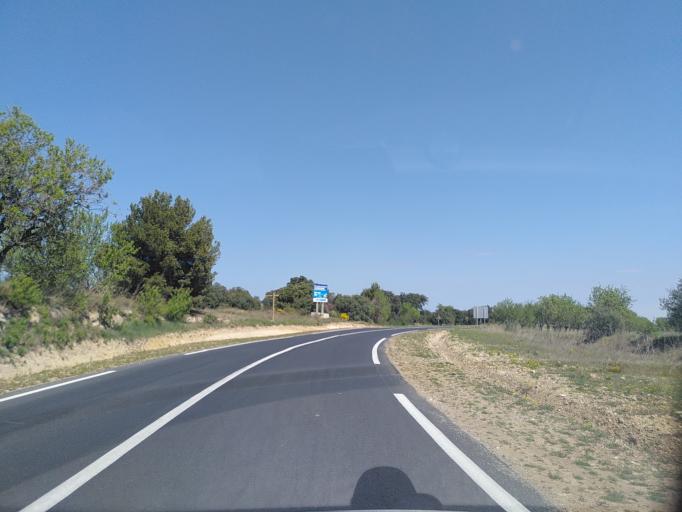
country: FR
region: Languedoc-Roussillon
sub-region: Departement de l'Aude
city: Ferrals-les-Corbieres
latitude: 43.1538
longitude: 2.7163
